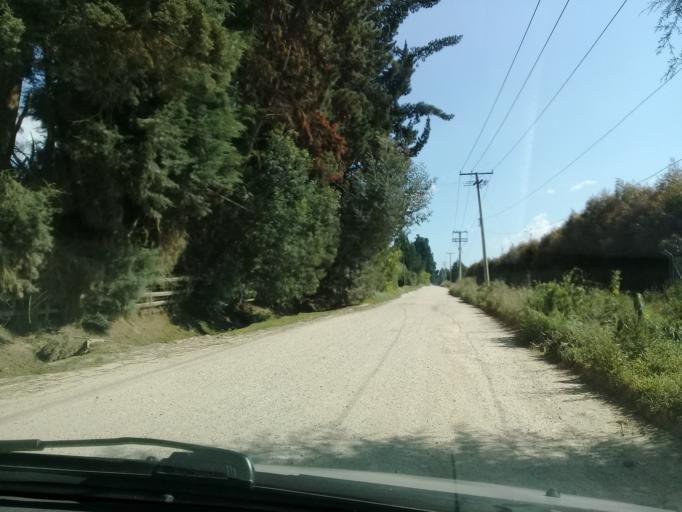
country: CO
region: Cundinamarca
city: Funza
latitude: 4.7507
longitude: -74.2055
